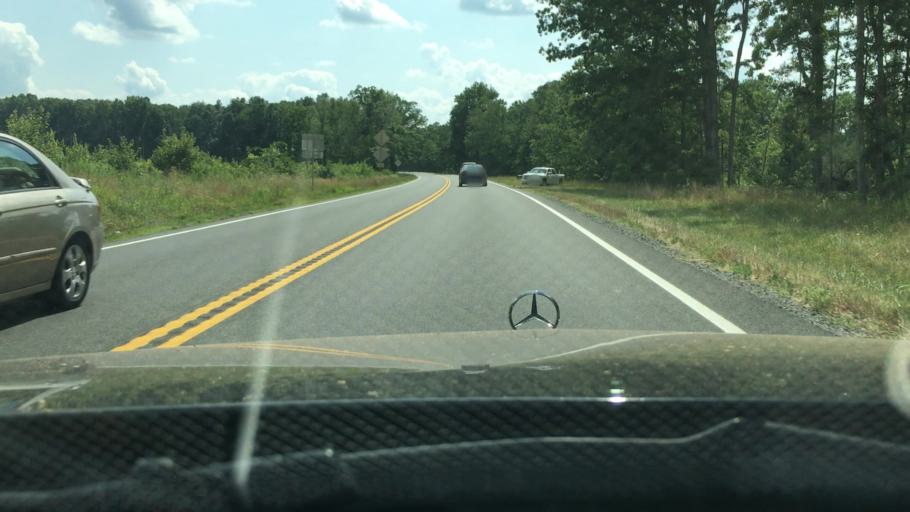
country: US
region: Virginia
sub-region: Culpeper County
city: Culpeper
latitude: 38.2860
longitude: -77.8687
